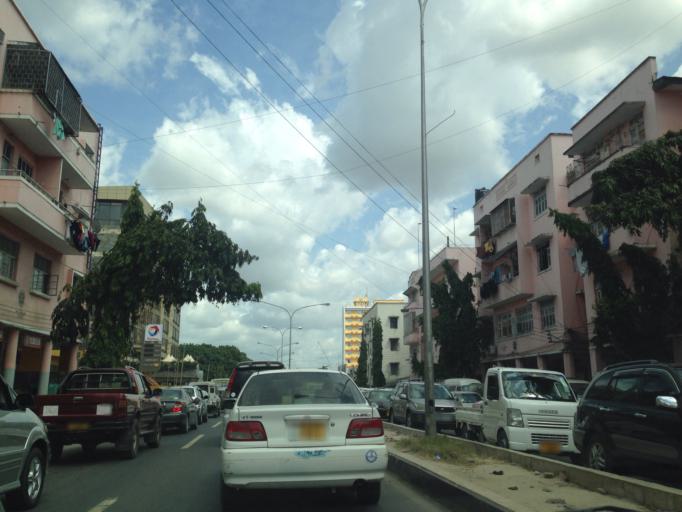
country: TZ
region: Dar es Salaam
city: Dar es Salaam
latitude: -6.8250
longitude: 39.2807
